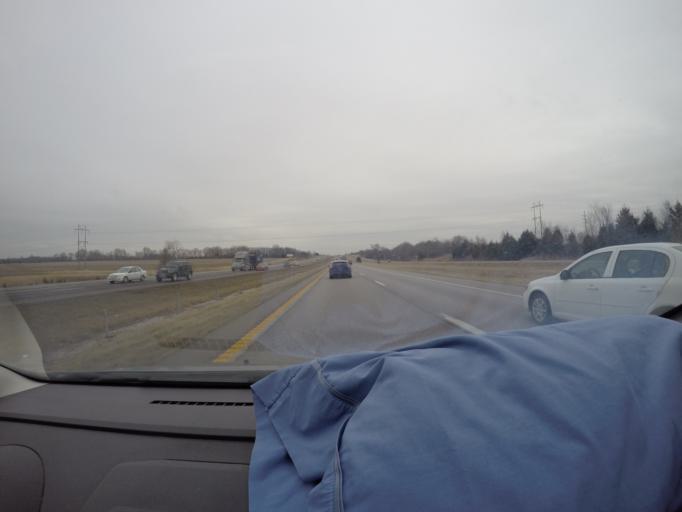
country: US
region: Missouri
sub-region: Warren County
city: Wright City
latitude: 38.8241
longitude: -90.9940
